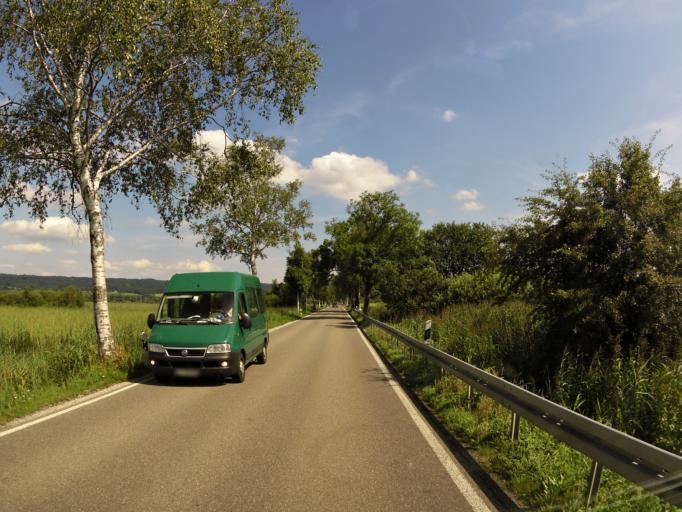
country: DE
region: Bavaria
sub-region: Upper Bavaria
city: Diessen am Ammersee
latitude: 47.9324
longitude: 11.1273
